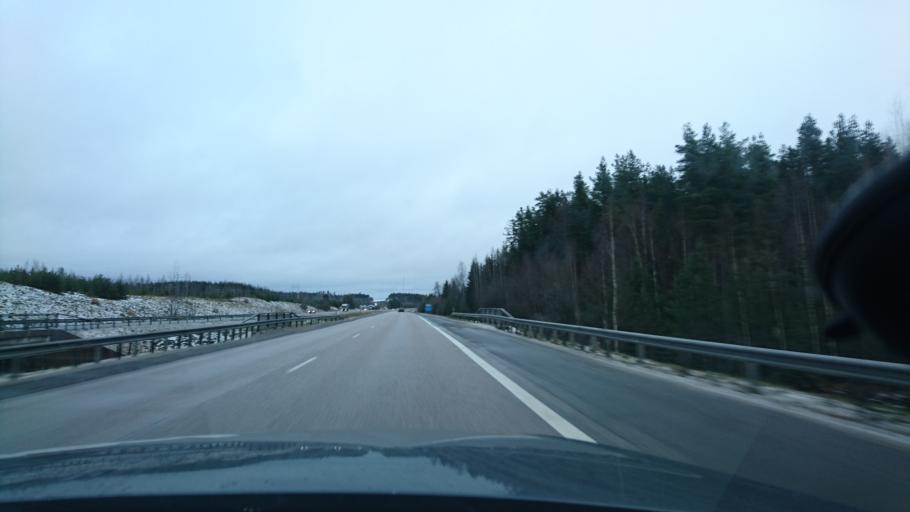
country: FI
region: Uusimaa
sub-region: Helsinki
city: Maentsaelae
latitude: 60.5853
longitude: 25.2251
